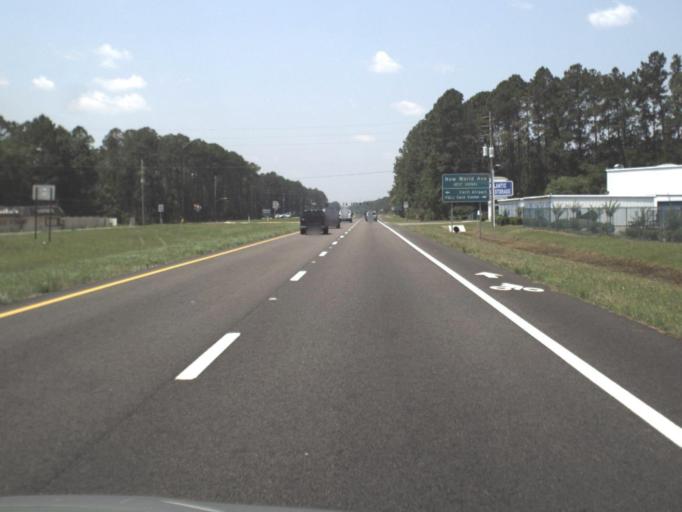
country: US
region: Florida
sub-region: Duval County
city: Baldwin
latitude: 30.2511
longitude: -81.8824
